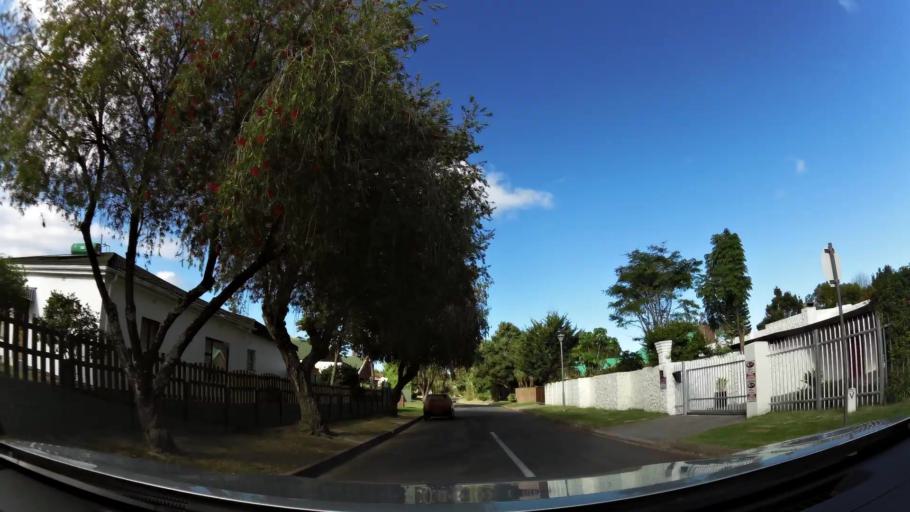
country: ZA
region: Western Cape
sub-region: Eden District Municipality
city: George
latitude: -33.9612
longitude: 22.4812
